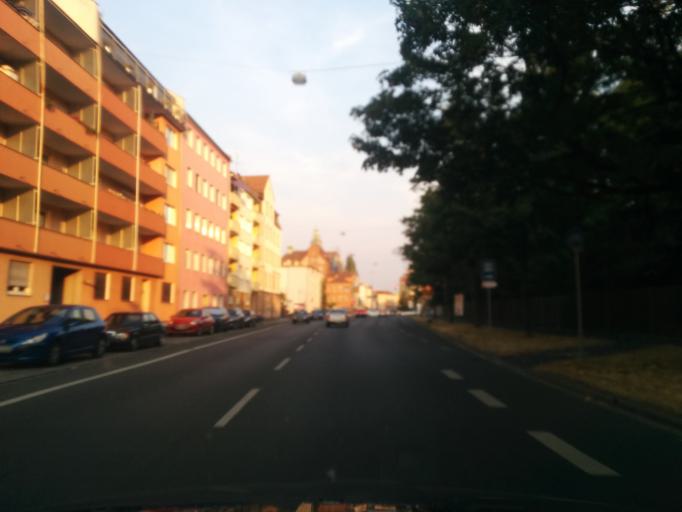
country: DE
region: Bavaria
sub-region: Regierungsbezirk Mittelfranken
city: Wetzendorf
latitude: 49.4639
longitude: 11.0497
